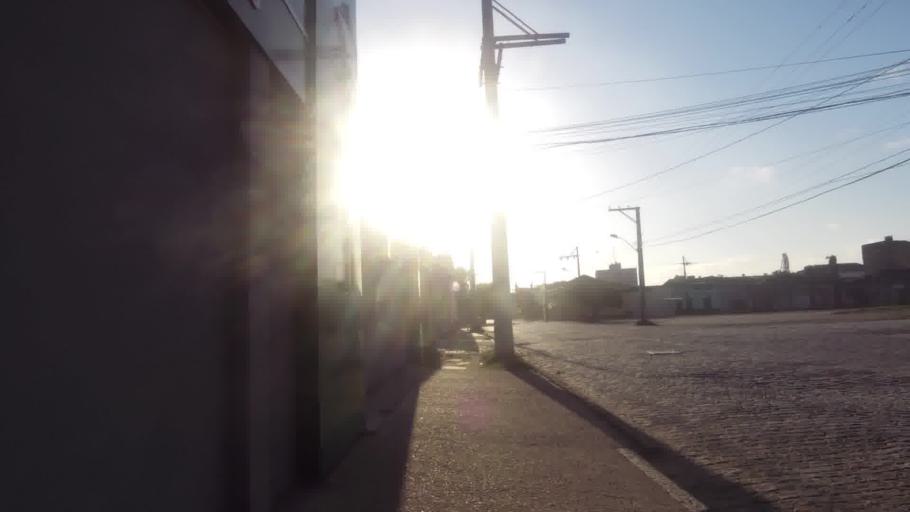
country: BR
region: Rio Grande do Sul
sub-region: Rio Grande
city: Rio Grande
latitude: -32.0317
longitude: -52.0873
